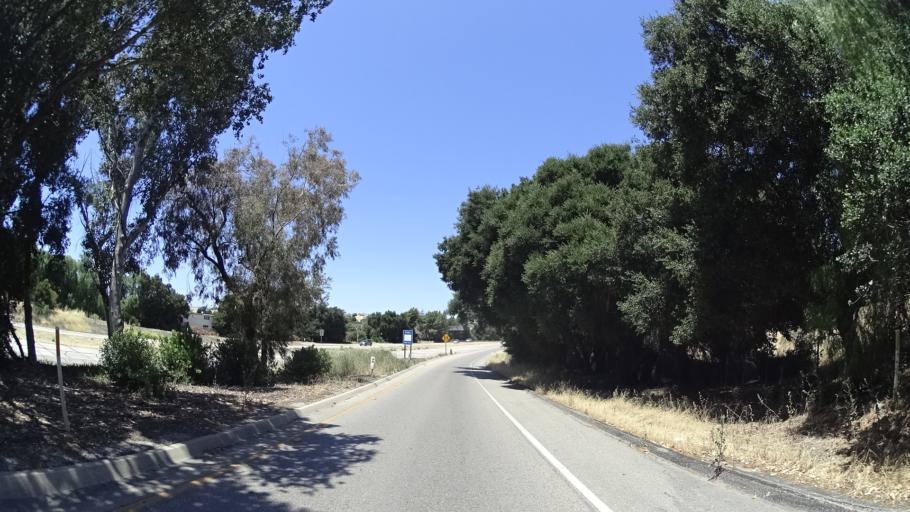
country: US
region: California
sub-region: Santa Barbara County
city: Buellton
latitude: 34.6125
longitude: -120.1896
